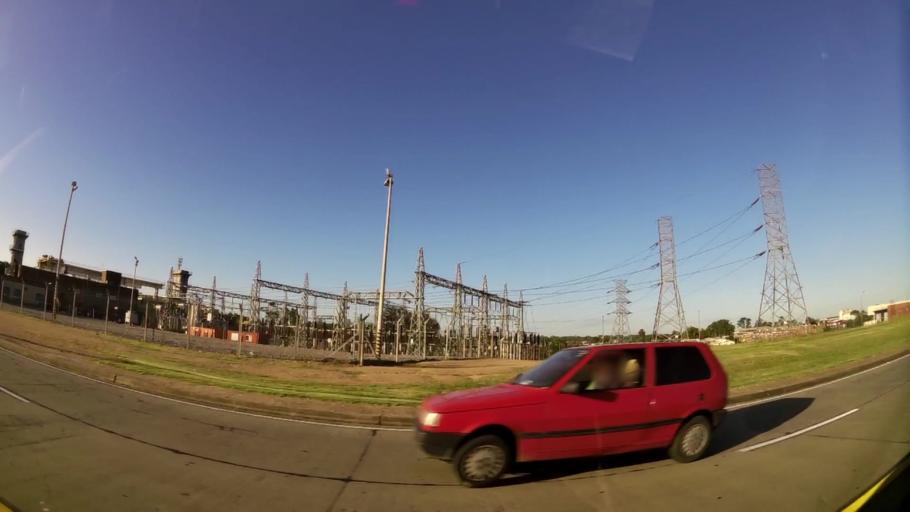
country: UY
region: Canelones
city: La Paz
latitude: -34.8279
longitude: -56.2351
